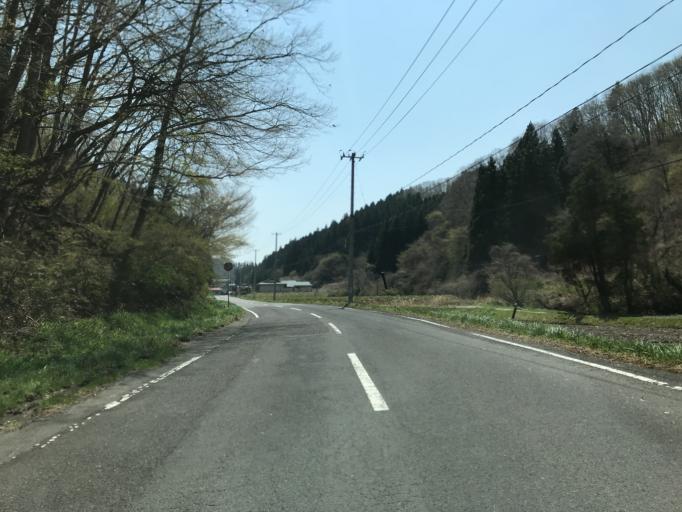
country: JP
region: Fukushima
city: Ishikawa
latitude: 37.0542
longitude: 140.4636
